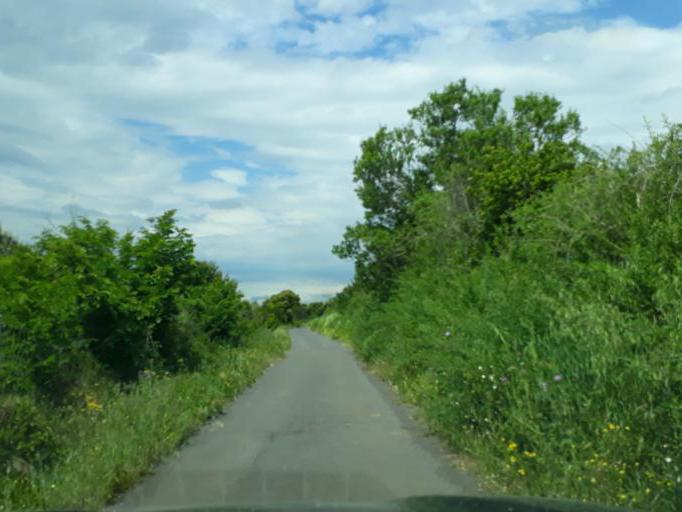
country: FR
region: Languedoc-Roussillon
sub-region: Departement de l'Herault
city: Agde
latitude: 43.2900
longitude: 3.4905
